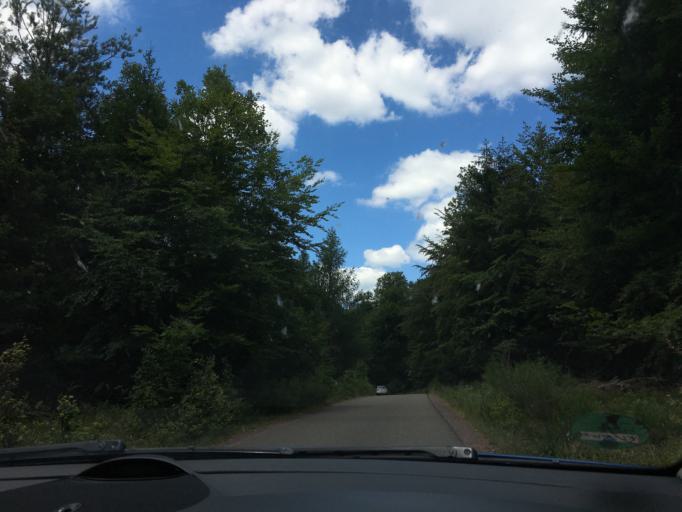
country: DE
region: Rheinland-Pfalz
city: Leimen
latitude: 49.2598
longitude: 7.8288
